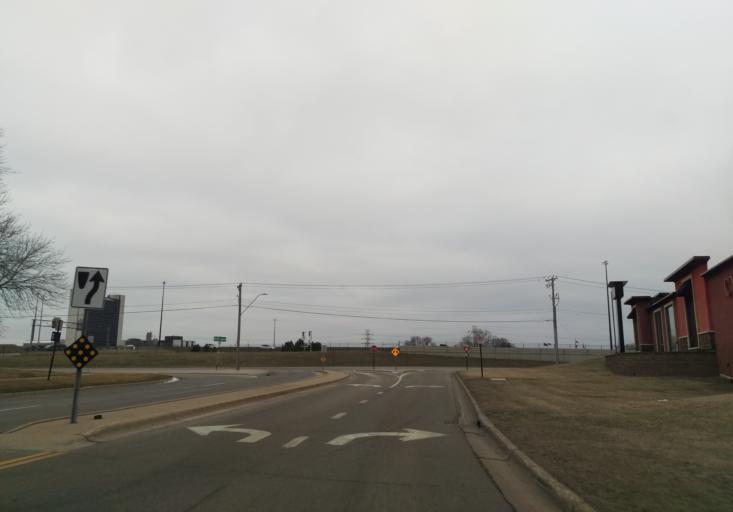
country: US
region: Minnesota
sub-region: Hennepin County
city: Edina
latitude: 44.8573
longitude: -93.3477
